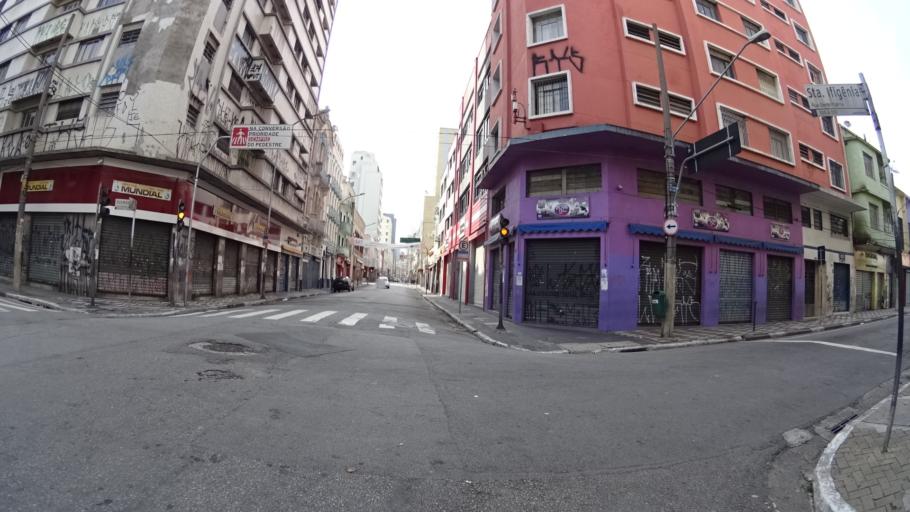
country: BR
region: Sao Paulo
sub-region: Sao Paulo
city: Sao Paulo
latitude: -23.5373
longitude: -46.6401
